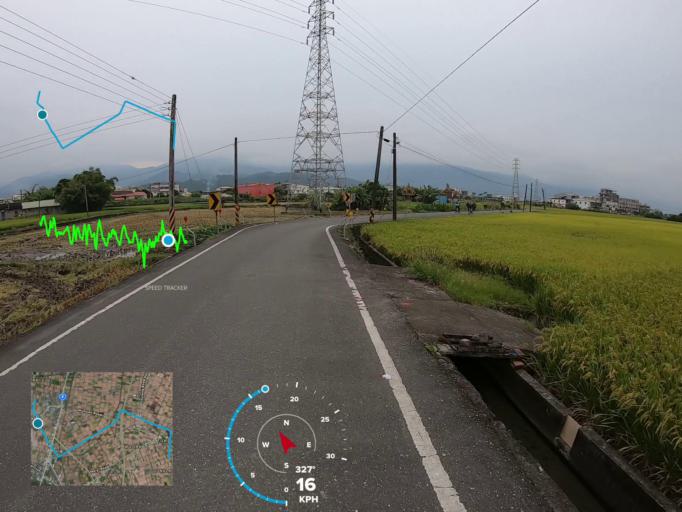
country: TW
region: Taiwan
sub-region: Yilan
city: Yilan
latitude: 24.7811
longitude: 121.7629
